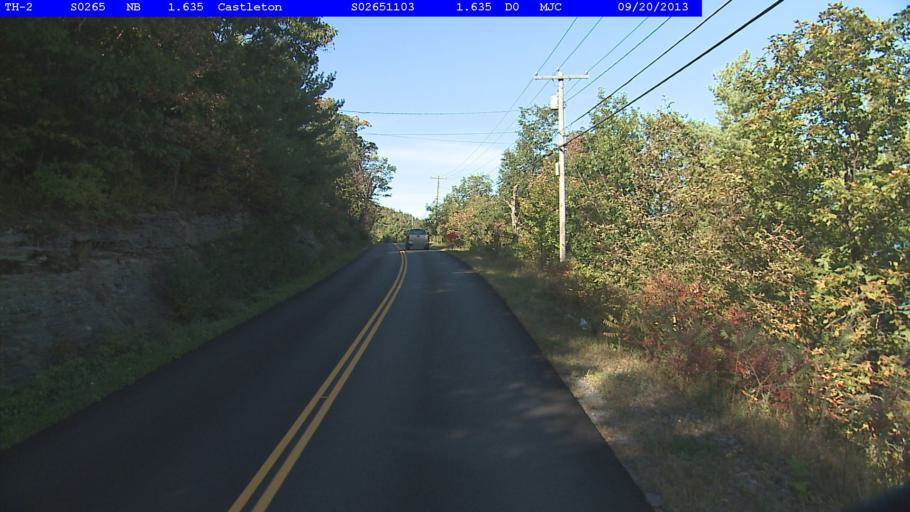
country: US
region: Vermont
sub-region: Rutland County
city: Fair Haven
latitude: 43.6262
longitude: -73.2329
